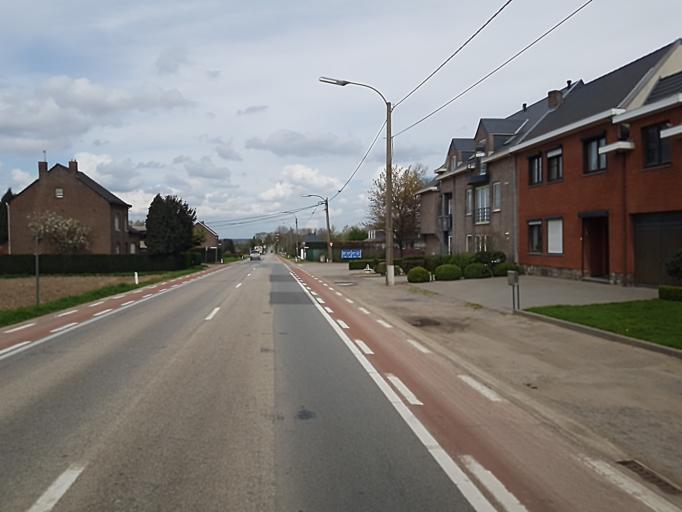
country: BE
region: Flanders
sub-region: Provincie Limburg
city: Riemst
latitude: 50.8420
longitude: 5.6254
